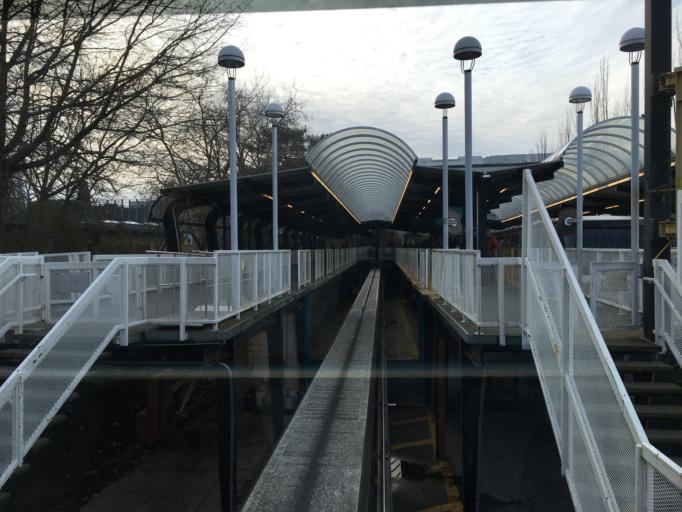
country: US
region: Washington
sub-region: King County
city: Seattle
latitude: 47.6213
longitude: -122.3490
